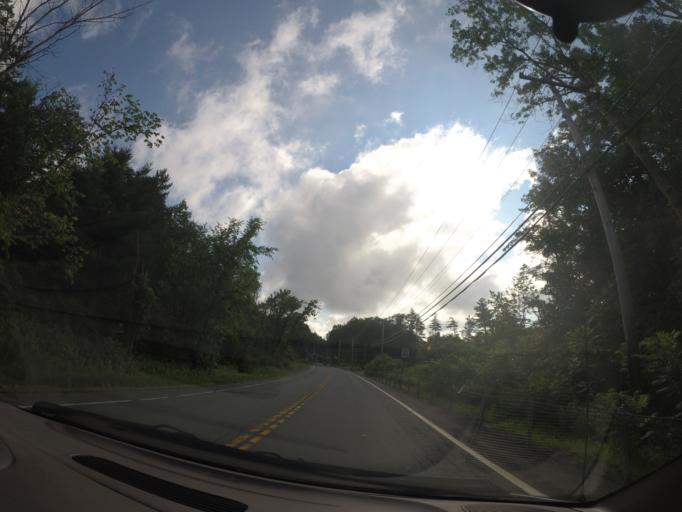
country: US
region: New York
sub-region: Rensselaer County
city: Poestenkill
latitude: 42.8235
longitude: -73.5060
